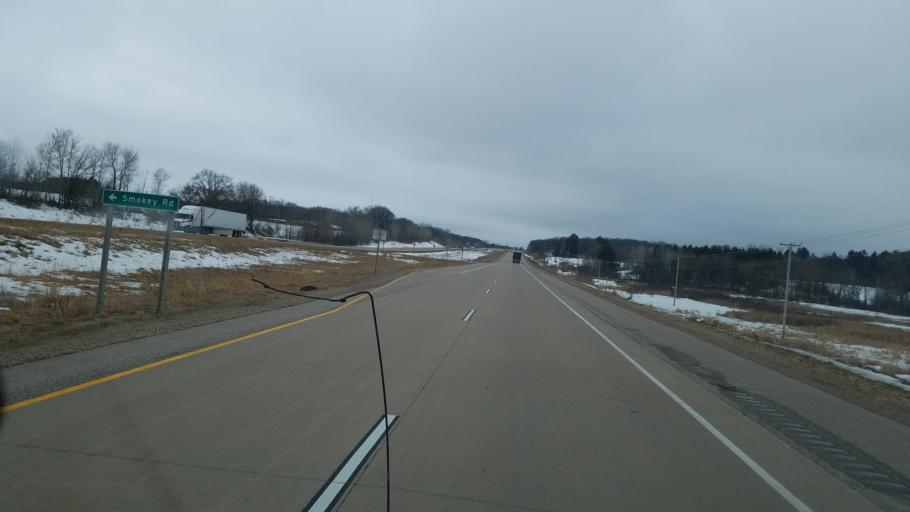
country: US
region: Wisconsin
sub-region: Portage County
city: Amherst
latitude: 44.5017
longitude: -89.3849
